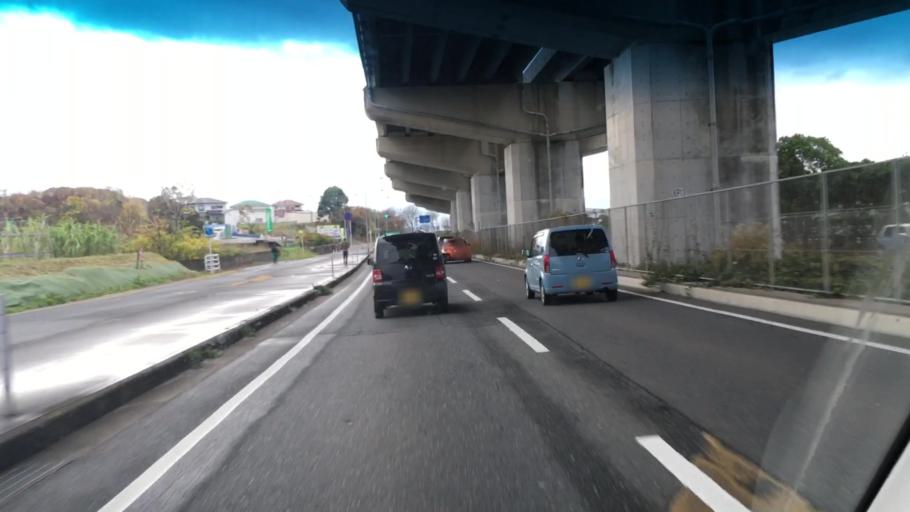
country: JP
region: Fukuoka
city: Maebaru-chuo
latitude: 33.5691
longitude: 130.2484
